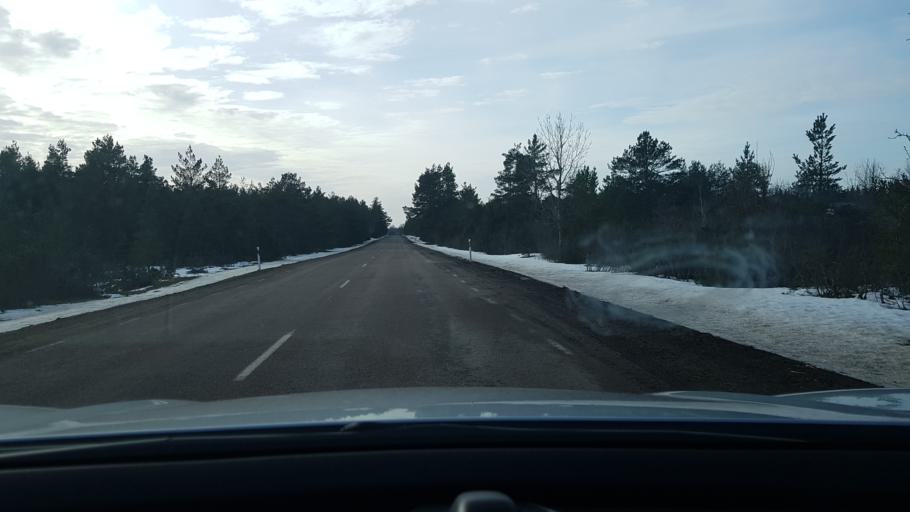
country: EE
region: Saare
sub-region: Kuressaare linn
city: Kuressaare
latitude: 58.3246
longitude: 22.5536
